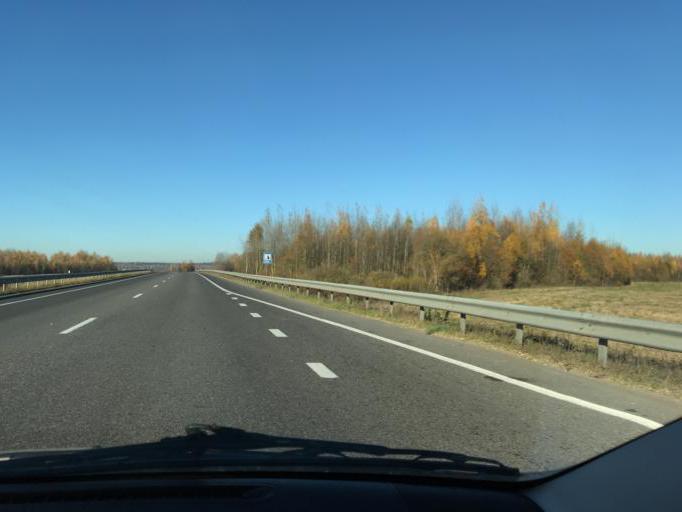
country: BY
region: Vitebsk
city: Vitebsk
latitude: 55.1041
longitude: 30.2339
